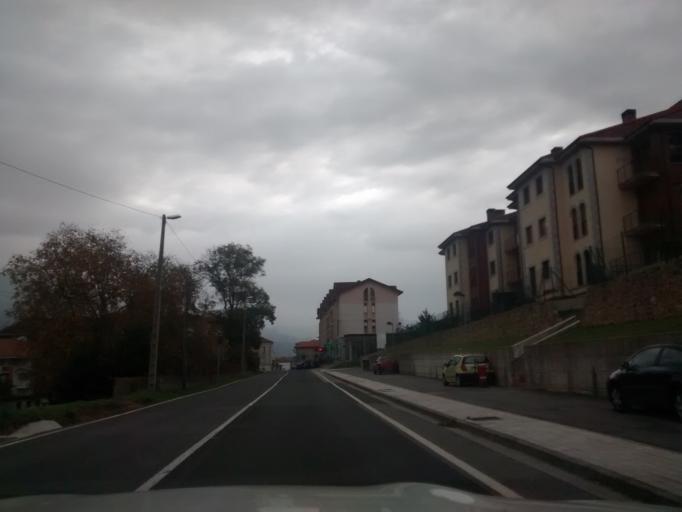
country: ES
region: Cantabria
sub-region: Provincia de Cantabria
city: Santiurde de Toranzo
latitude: 43.1989
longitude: -3.9258
